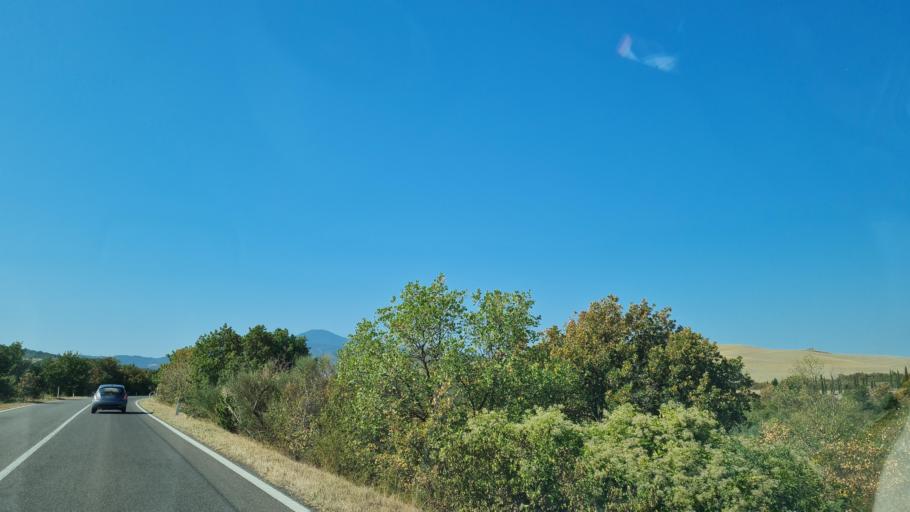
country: IT
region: Tuscany
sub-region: Provincia di Siena
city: Chianciano Terme
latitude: 43.0042
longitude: 11.7299
